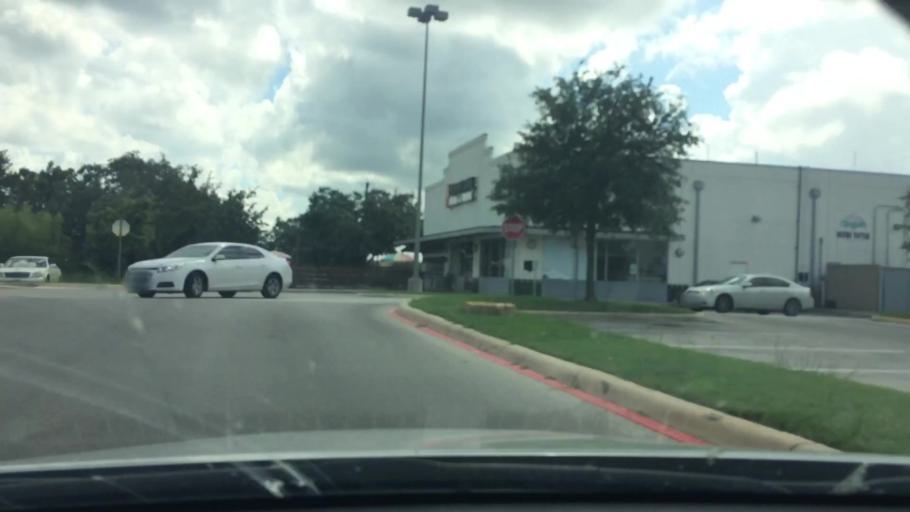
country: US
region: Texas
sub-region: Bexar County
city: San Antonio
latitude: 29.3531
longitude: -98.4506
